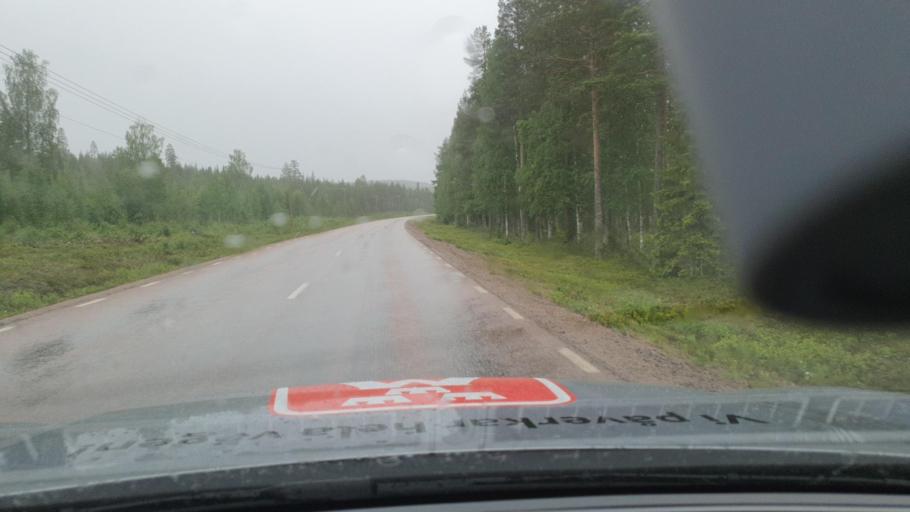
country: SE
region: Norrbotten
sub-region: Overkalix Kommun
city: OEverkalix
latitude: 66.4209
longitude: 22.9643
